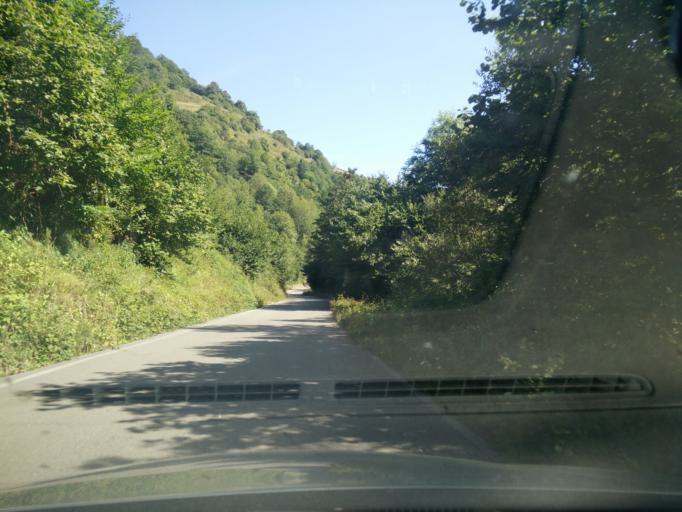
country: ES
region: Asturias
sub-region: Province of Asturias
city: Campo de Caso
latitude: 43.1835
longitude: -5.3882
